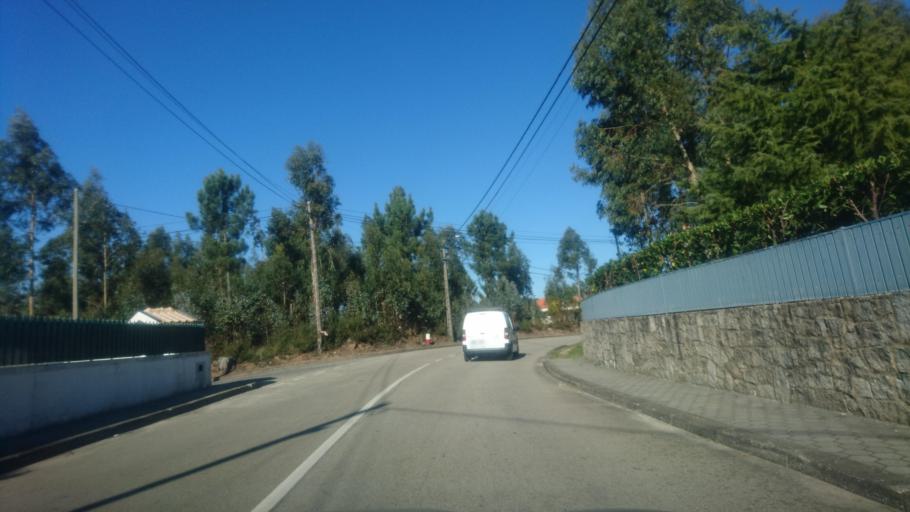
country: PT
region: Aveiro
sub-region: Oliveira de Azemeis
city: Sao Roque
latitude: 40.8758
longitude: -8.4651
